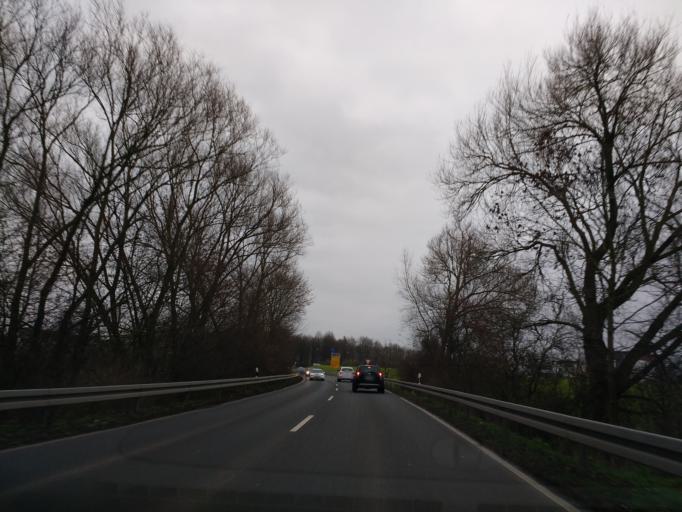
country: DE
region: Hesse
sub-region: Regierungsbezirk Kassel
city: Baunatal
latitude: 51.2605
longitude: 9.3935
